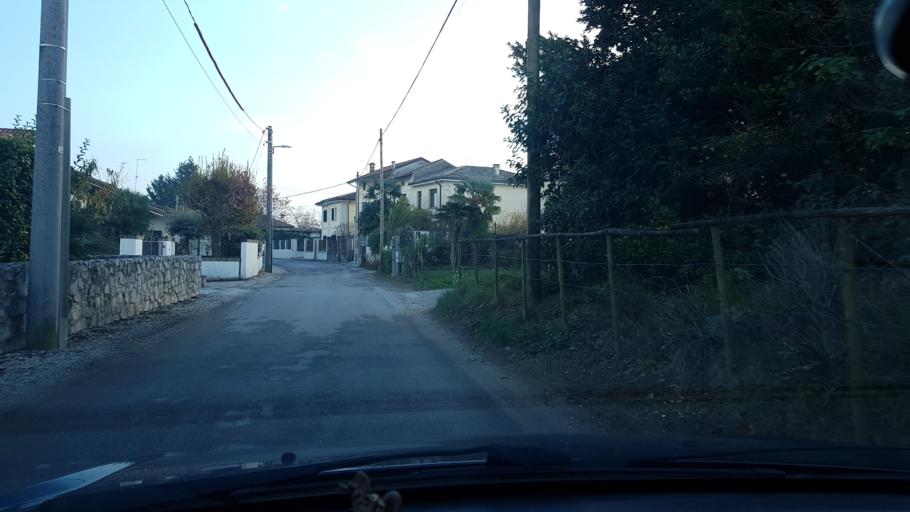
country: IT
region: Friuli Venezia Giulia
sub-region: Provincia di Gorizia
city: Ronchi dei Legionari
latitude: 45.8354
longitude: 13.5047
